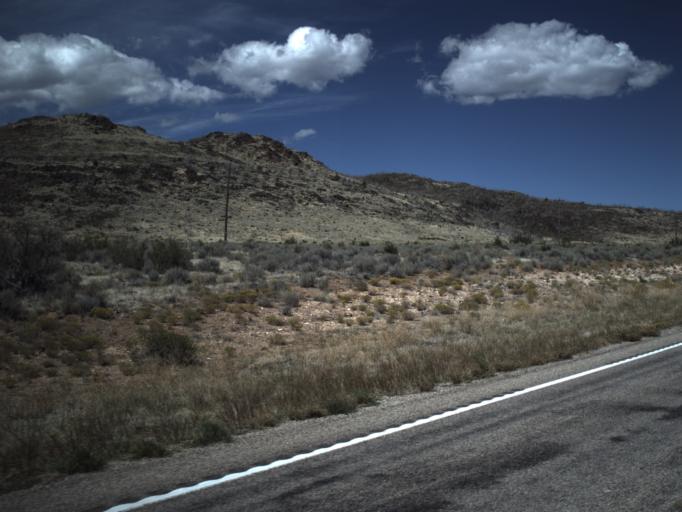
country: US
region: Utah
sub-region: Washington County
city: Enterprise
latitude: 37.3815
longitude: -113.6526
